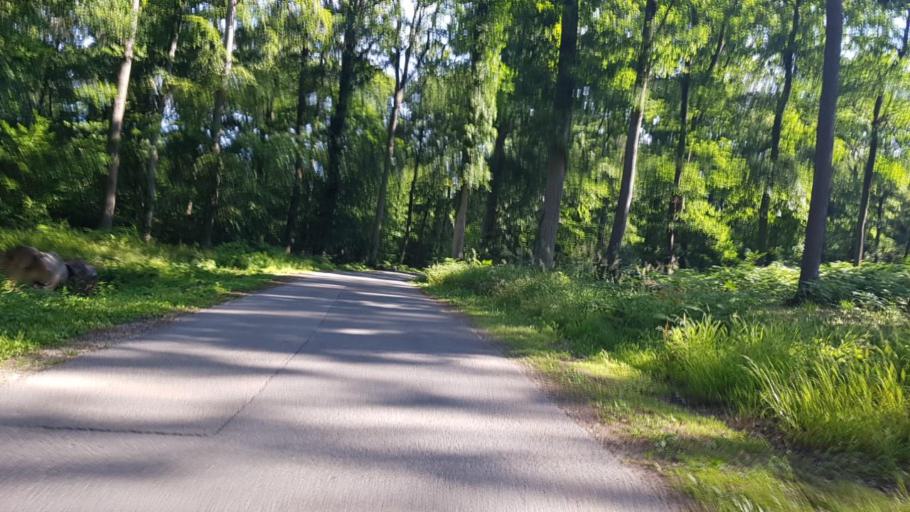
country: FR
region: Picardie
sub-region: Departement de l'Oise
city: Pont-Sainte-Maxence
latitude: 49.2727
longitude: 2.6185
